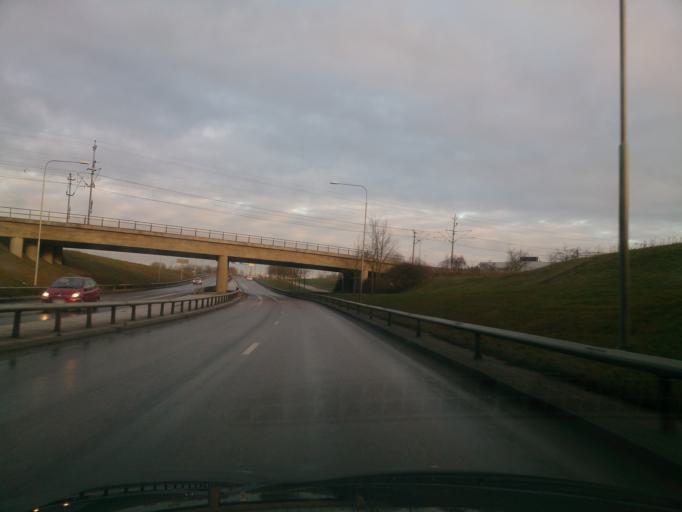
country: SE
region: OEstergoetland
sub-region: Linkopings Kommun
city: Linkoping
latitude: 58.4141
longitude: 15.6545
